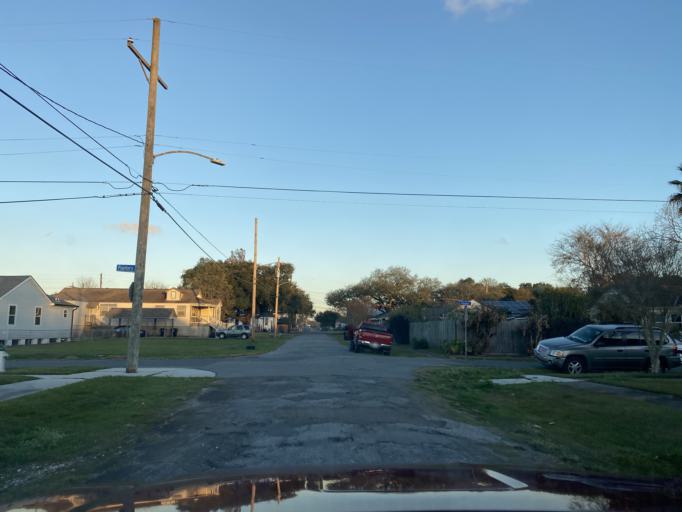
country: US
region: Louisiana
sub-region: Orleans Parish
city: New Orleans
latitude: 30.0204
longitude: -90.0531
